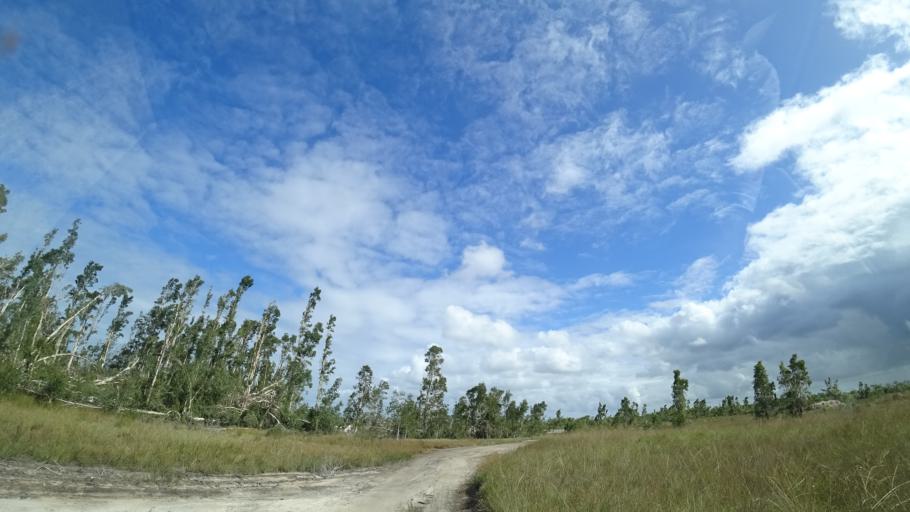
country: MZ
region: Sofala
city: Beira
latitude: -19.5757
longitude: 35.2557
